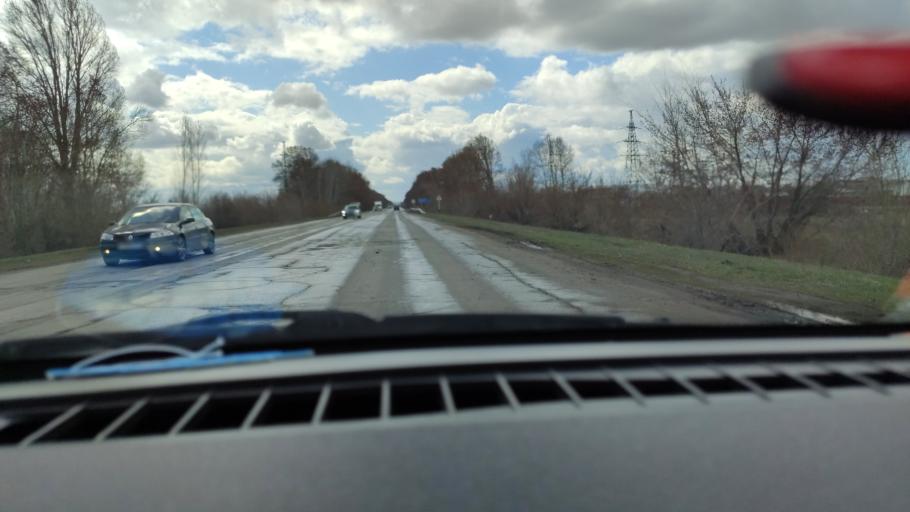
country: RU
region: Samara
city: Tol'yatti
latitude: 53.6287
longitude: 49.4168
